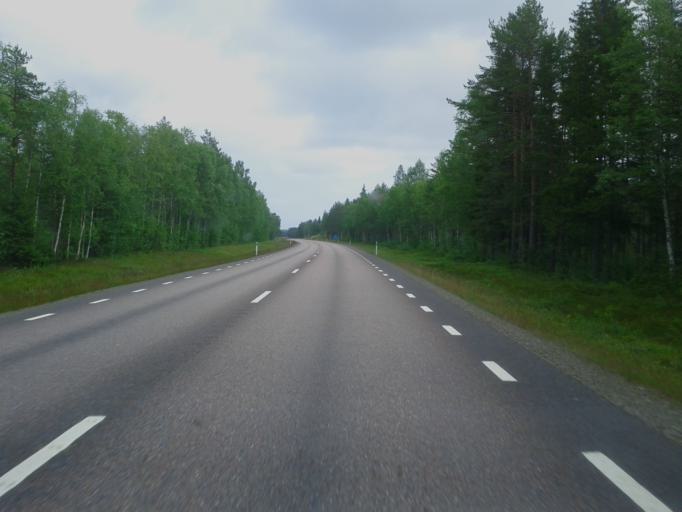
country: SE
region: Vaesterbotten
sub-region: Skelleftea Kommun
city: Burea
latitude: 64.3210
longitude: 21.1808
